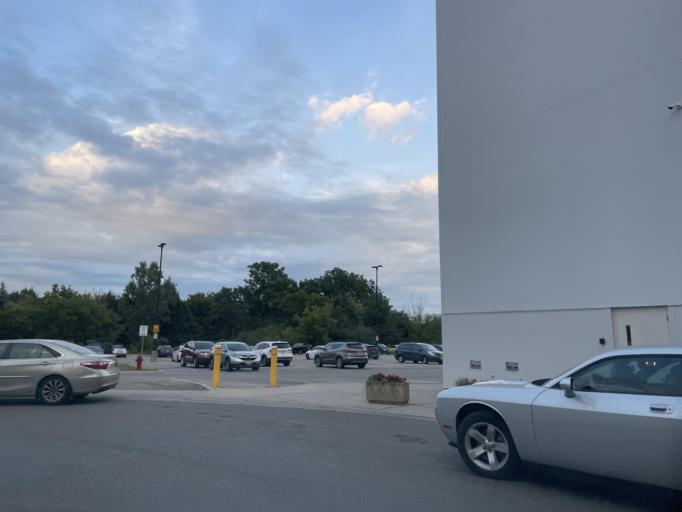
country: CA
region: Ontario
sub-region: Wellington County
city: Guelph
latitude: 43.5566
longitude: -80.2537
